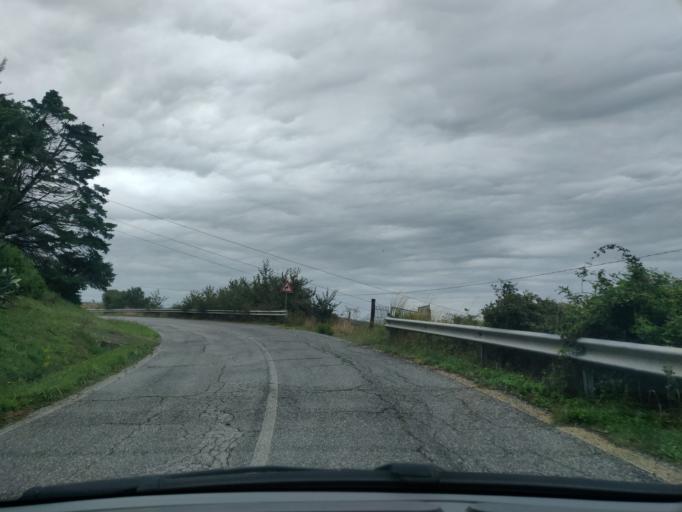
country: IT
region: Latium
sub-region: Citta metropolitana di Roma Capitale
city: Aurelia
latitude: 42.1328
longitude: 11.8408
